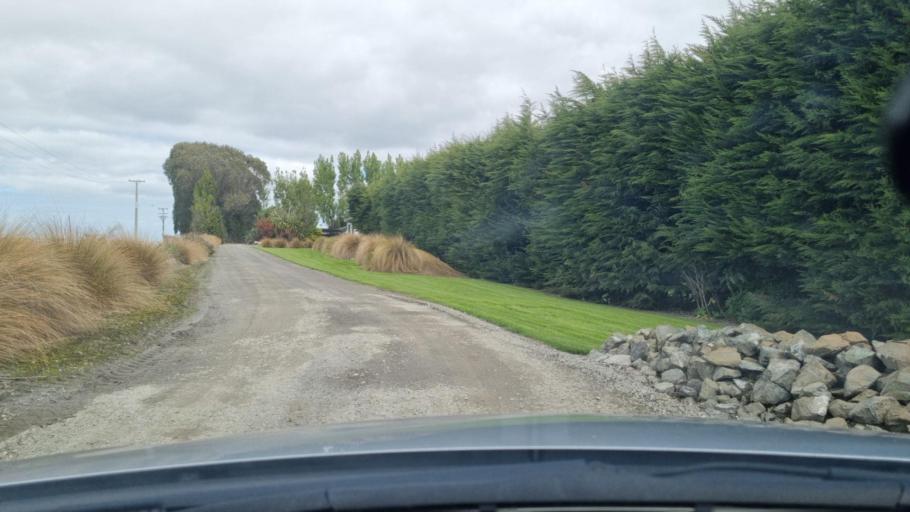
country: NZ
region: Southland
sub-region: Invercargill City
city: Invercargill
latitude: -46.4558
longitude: 168.4495
